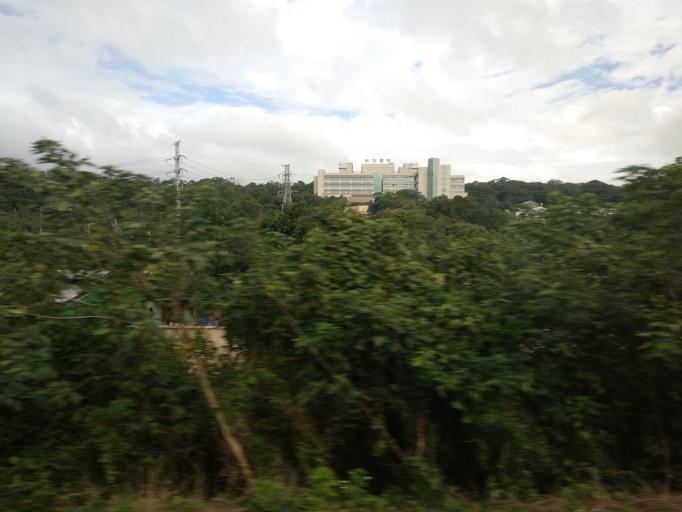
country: TW
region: Taiwan
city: Daxi
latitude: 24.9139
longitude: 121.1551
